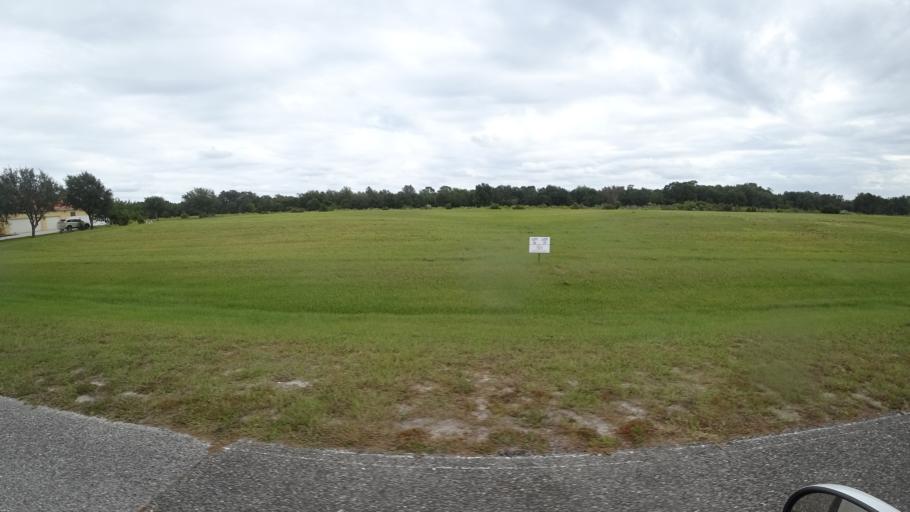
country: US
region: Florida
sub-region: Hillsborough County
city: Wimauma
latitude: 27.6516
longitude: -82.3242
